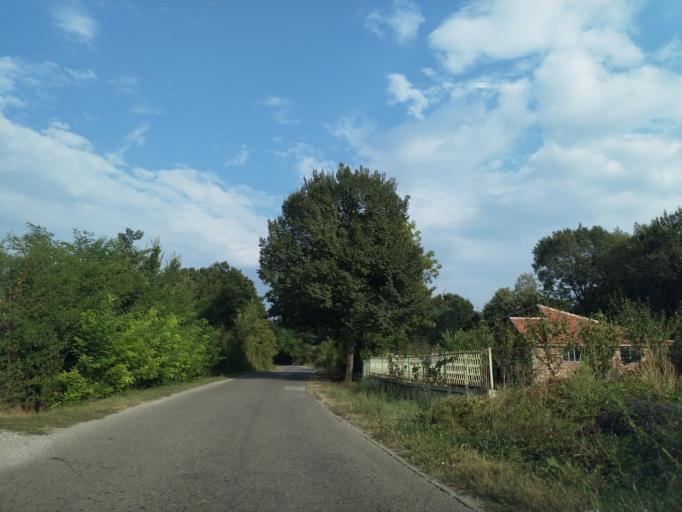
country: RS
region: Central Serbia
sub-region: Pomoravski Okrug
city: Paracin
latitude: 43.8493
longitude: 21.4508
